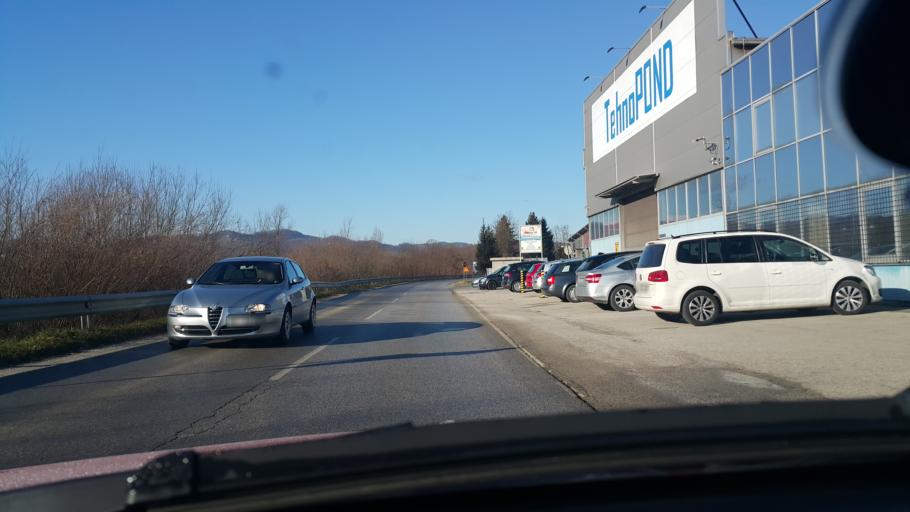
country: SI
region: Pesnica
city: Pesnica pri Mariboru
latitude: 46.6013
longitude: 15.6725
